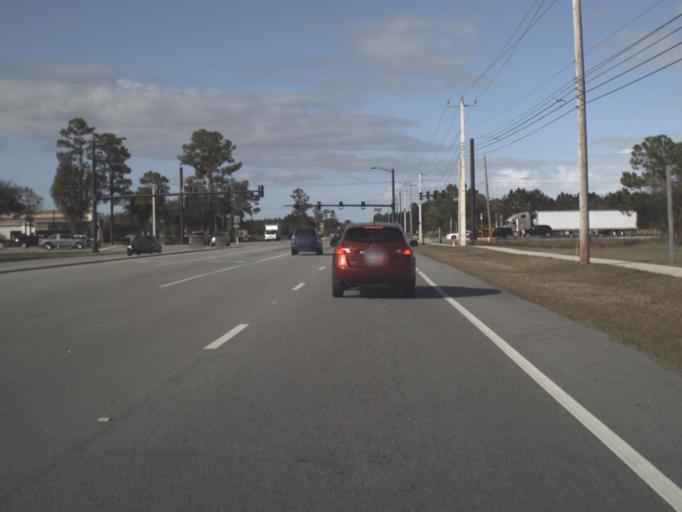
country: US
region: Florida
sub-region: Volusia County
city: Holly Hill
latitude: 29.2228
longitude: -81.0933
